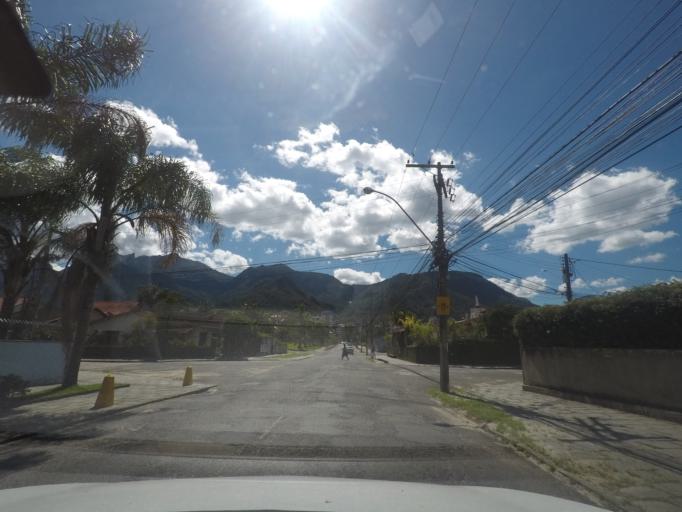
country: BR
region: Rio de Janeiro
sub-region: Teresopolis
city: Teresopolis
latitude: -22.4343
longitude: -42.9728
